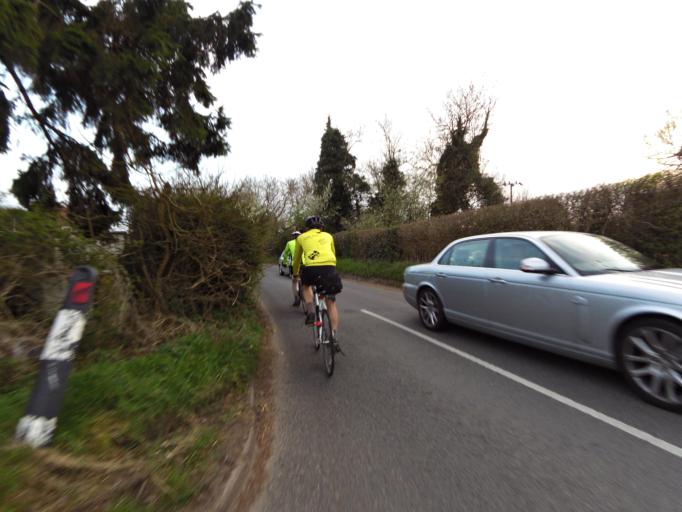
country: GB
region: England
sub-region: Suffolk
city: Kesgrave
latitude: 52.1372
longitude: 1.2352
